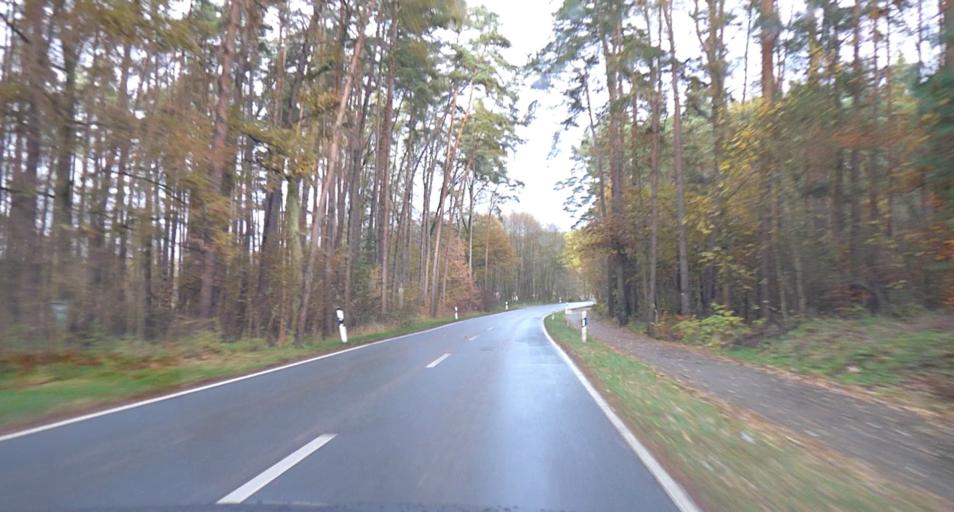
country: DE
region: Bavaria
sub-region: Upper Franconia
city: Langensendelbach
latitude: 49.6361
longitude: 11.0501
